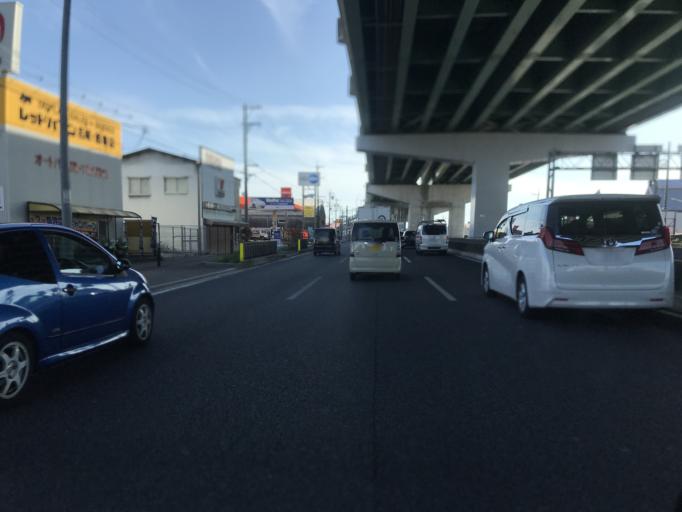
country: JP
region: Aichi
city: Iwakura
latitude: 35.2467
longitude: 136.8451
